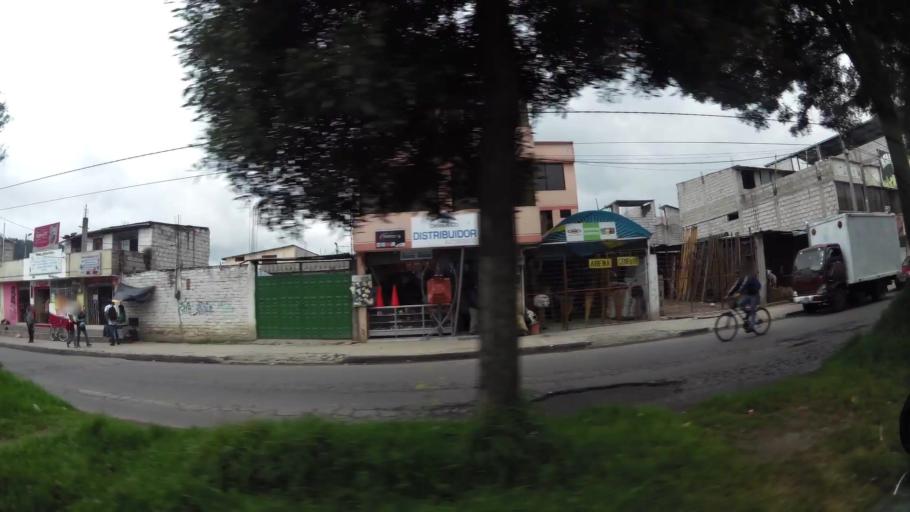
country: EC
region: Pichincha
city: Sangolqui
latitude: -0.3289
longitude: -78.5344
